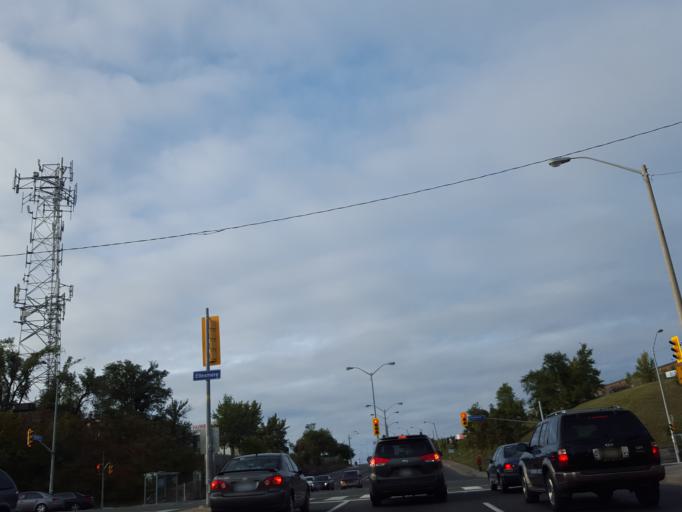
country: CA
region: Ontario
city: Scarborough
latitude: 43.7608
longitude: -79.3006
